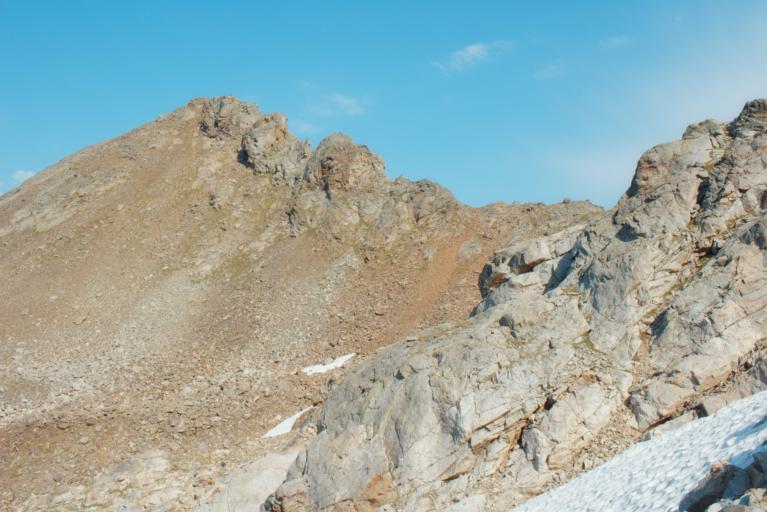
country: RU
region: Karachayevo-Cherkesiya
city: Nizhniy Arkhyz
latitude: 43.4586
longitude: 41.2248
